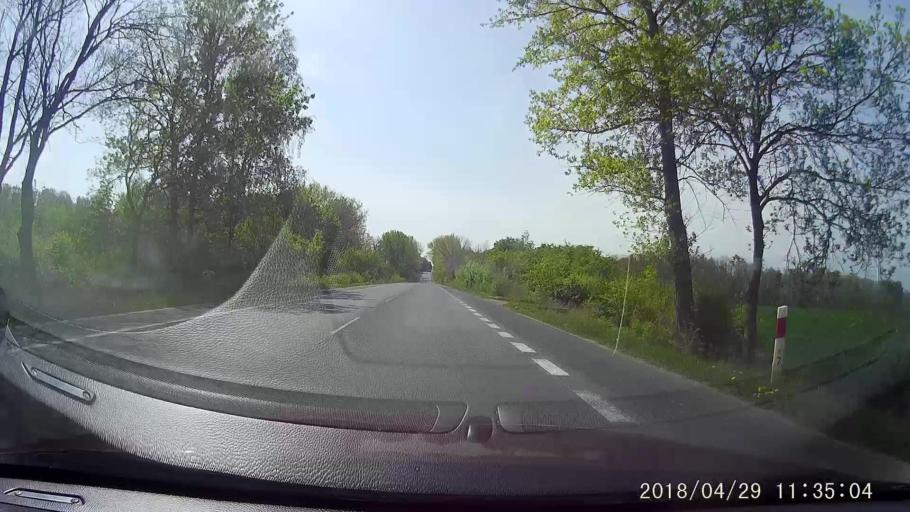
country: PL
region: Lower Silesian Voivodeship
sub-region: Powiat zgorzelecki
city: Sulikow
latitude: 51.0795
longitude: 15.0204
